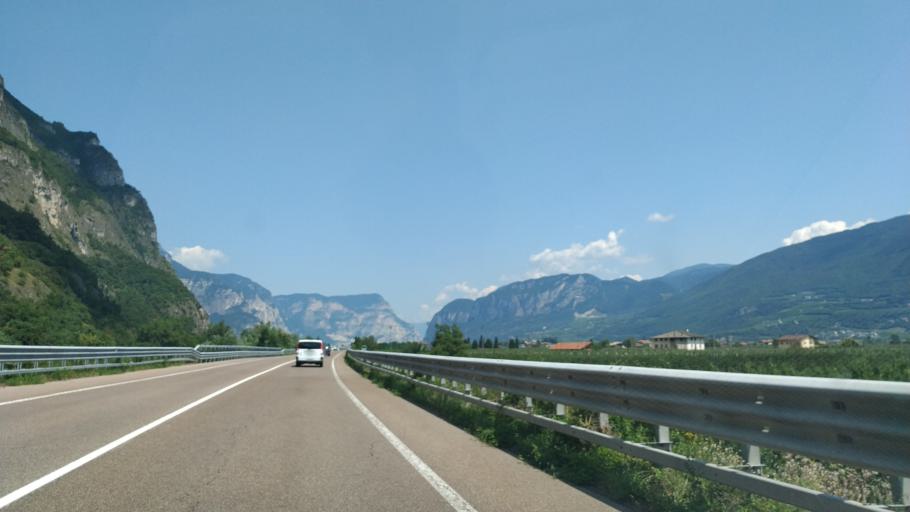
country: IT
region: Trentino-Alto Adige
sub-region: Provincia di Trento
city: Fai della Paganella
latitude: 46.1652
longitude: 11.0821
